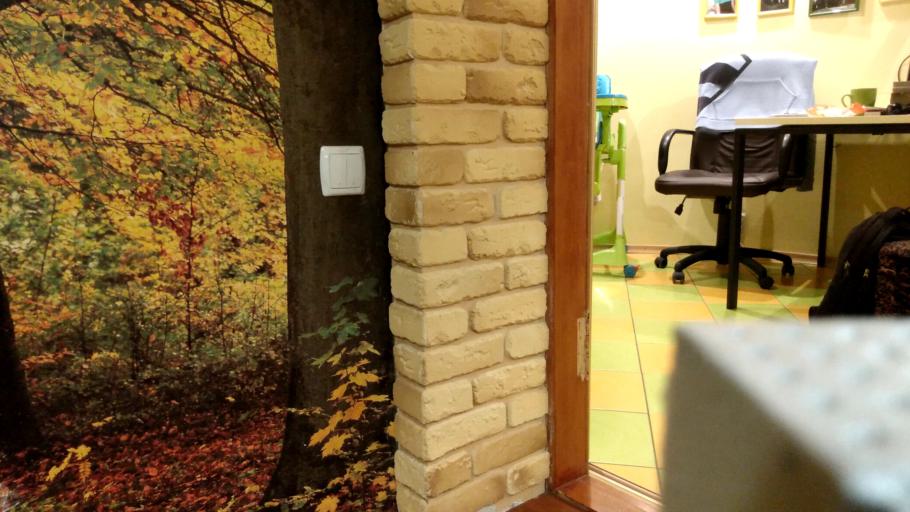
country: RU
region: Republic of Karelia
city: Pudozh
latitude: 61.7869
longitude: 37.6766
